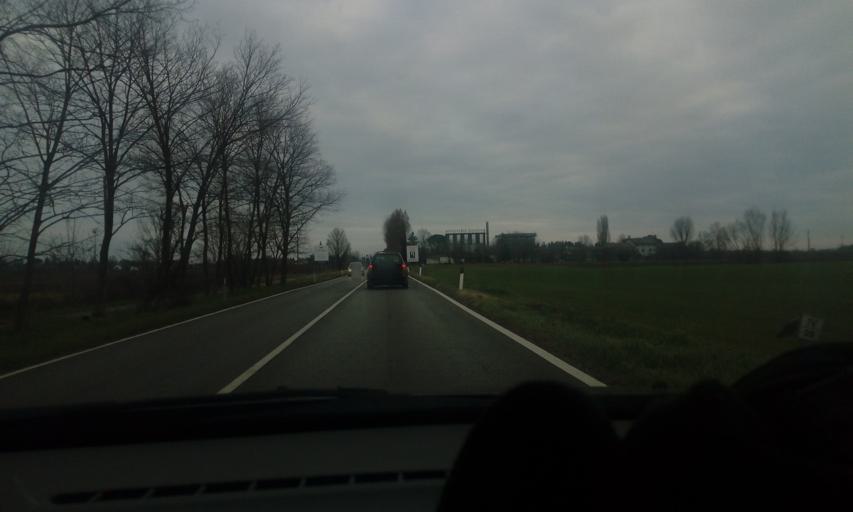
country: IT
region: Friuli Venezia Giulia
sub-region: Provincia di Udine
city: Aquileia
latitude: 45.7851
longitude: 13.3594
